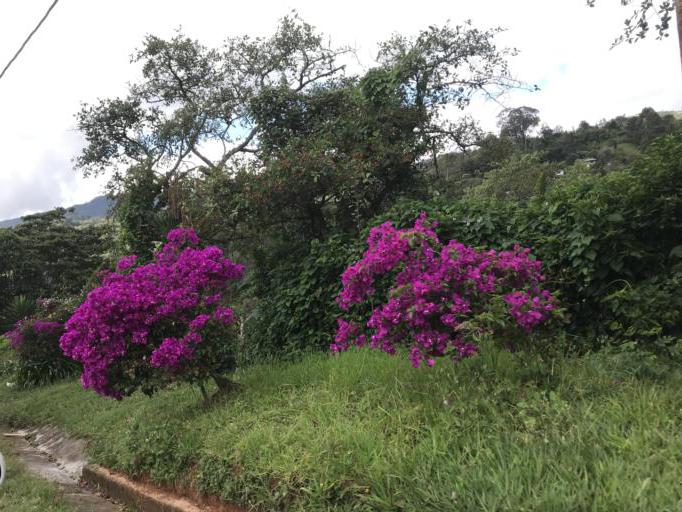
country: CO
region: Valle del Cauca
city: Cali
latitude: 3.5160
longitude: -76.6048
